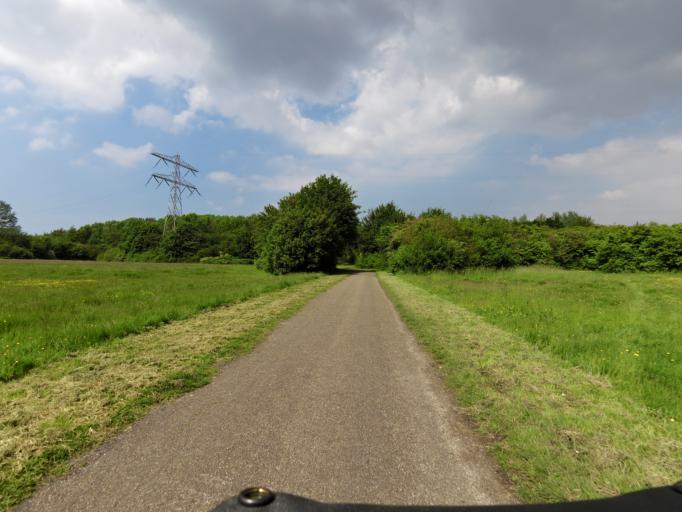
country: NL
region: South Holland
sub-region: Gemeente Maassluis
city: Maassluis
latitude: 51.8566
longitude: 4.2455
